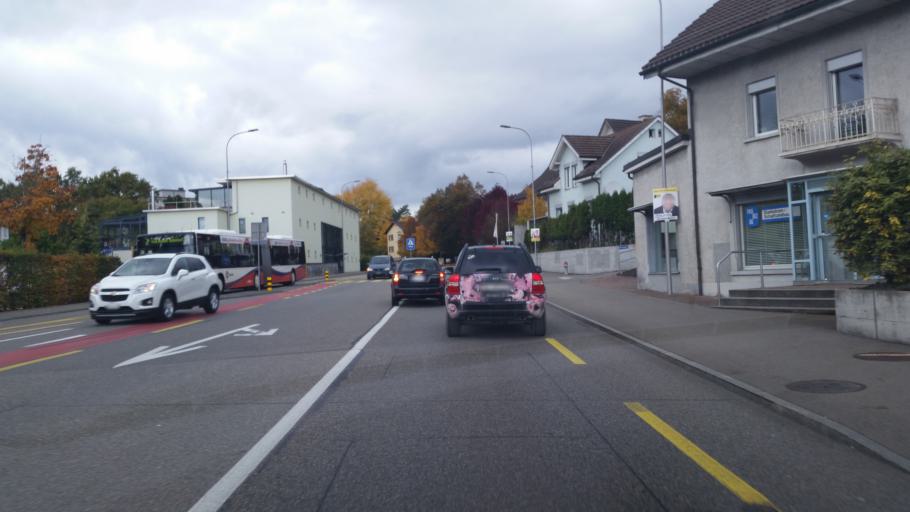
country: CH
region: Aargau
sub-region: Bezirk Baden
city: Obersiggenthal
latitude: 47.4852
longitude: 8.2991
